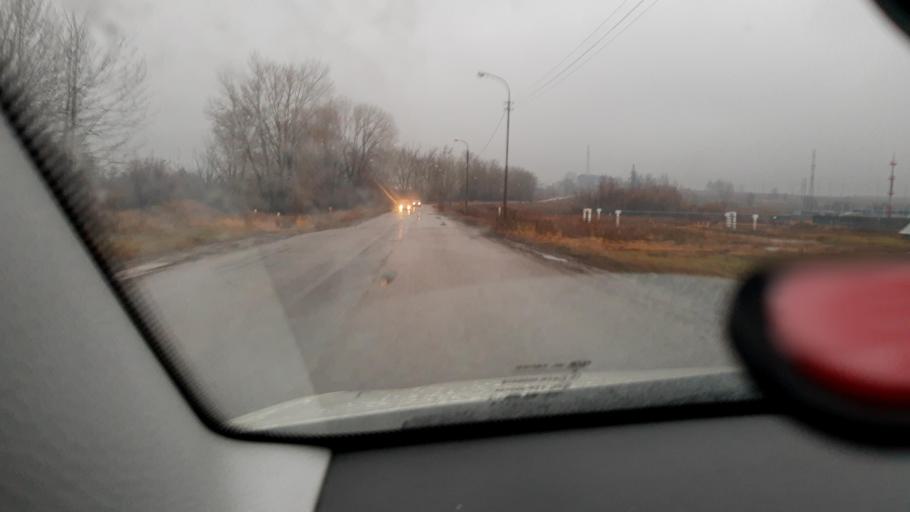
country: RU
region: Bashkortostan
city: Blagoveshchensk
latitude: 54.8998
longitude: 56.1570
